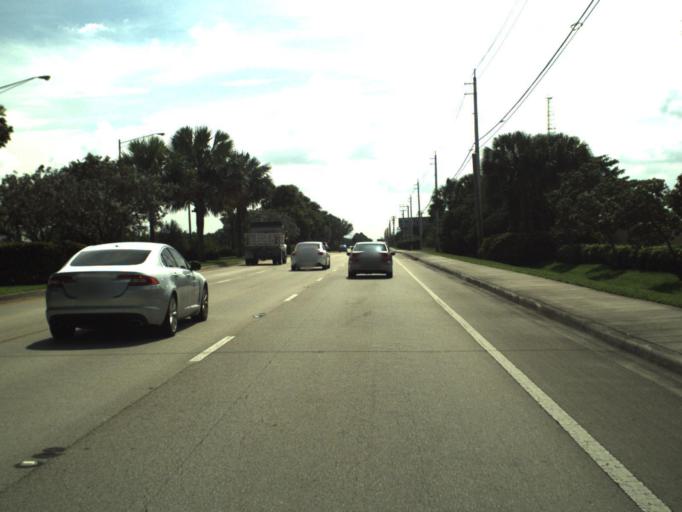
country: US
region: Florida
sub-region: Broward County
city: Cooper City
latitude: 26.0636
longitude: -80.3019
